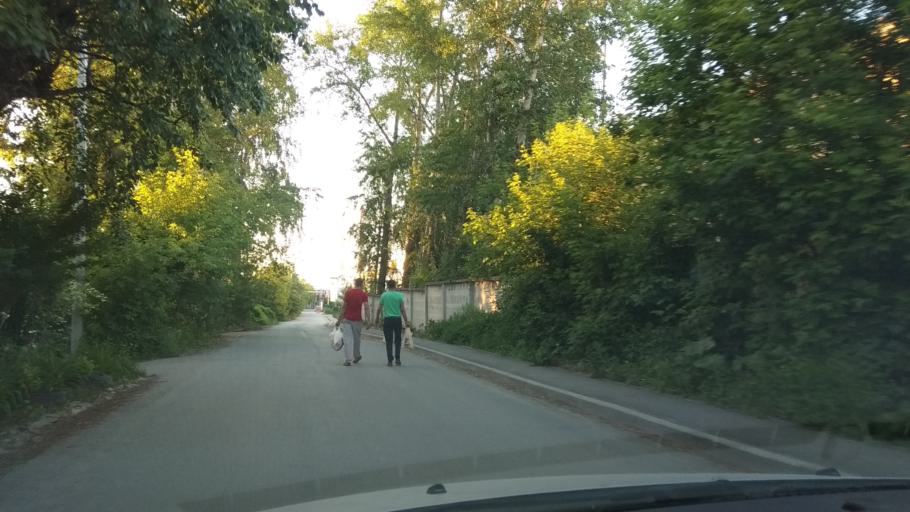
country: RU
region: Sverdlovsk
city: Sredneuralsk
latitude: 56.9895
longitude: 60.4573
